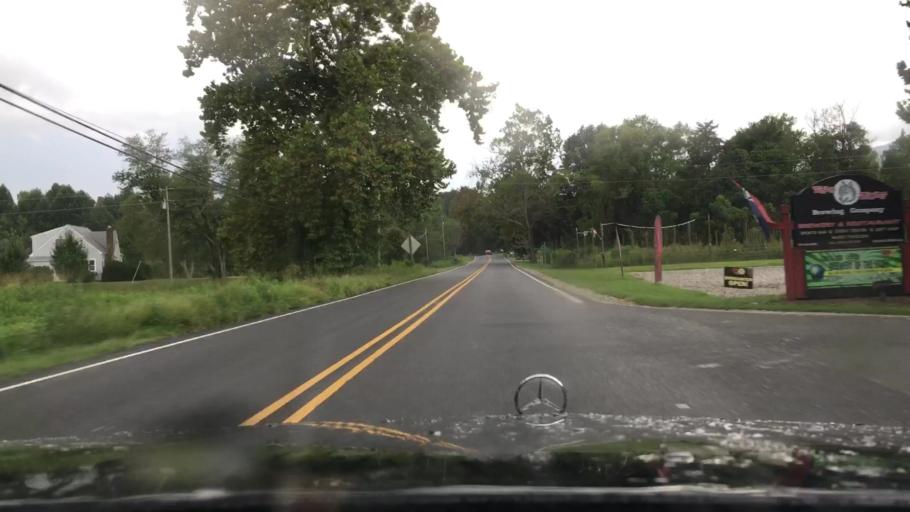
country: US
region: Virginia
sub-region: Nelson County
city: Nellysford
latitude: 37.8874
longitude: -78.8799
